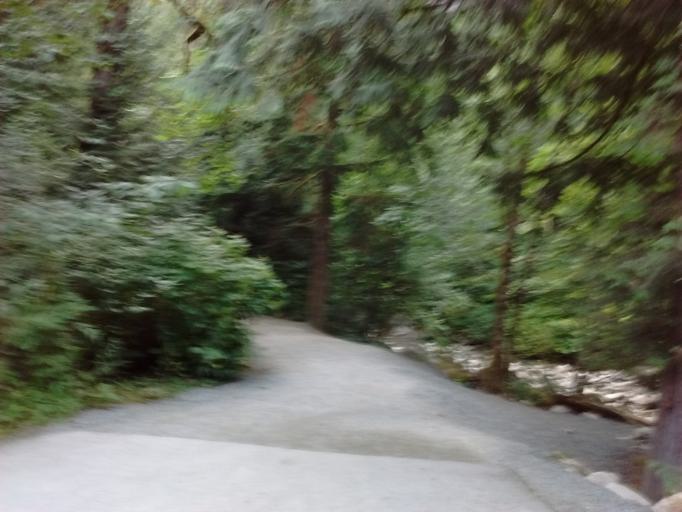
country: CA
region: British Columbia
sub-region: Greater Vancouver Regional District
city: Lions Bay
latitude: 49.6706
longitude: -123.1597
